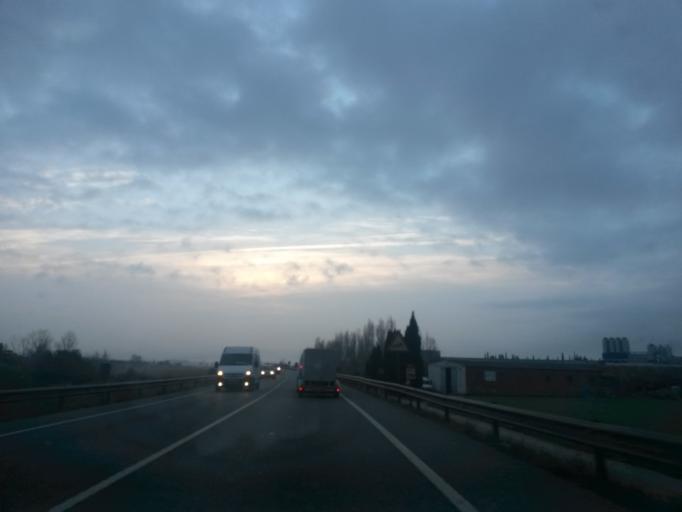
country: ES
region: Catalonia
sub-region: Provincia de Girona
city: Pont de Molins
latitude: 42.2926
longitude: 2.9461
